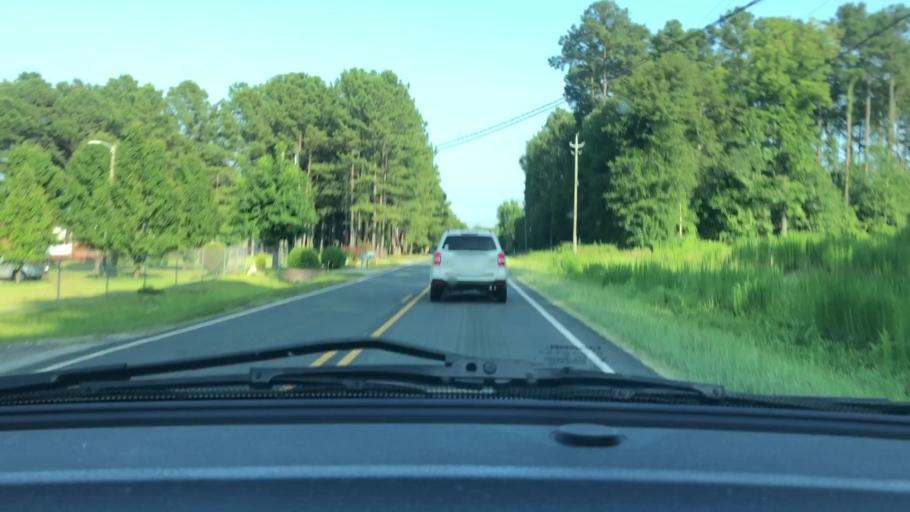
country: US
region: North Carolina
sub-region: Lee County
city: Broadway
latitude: 35.3580
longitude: -79.0815
